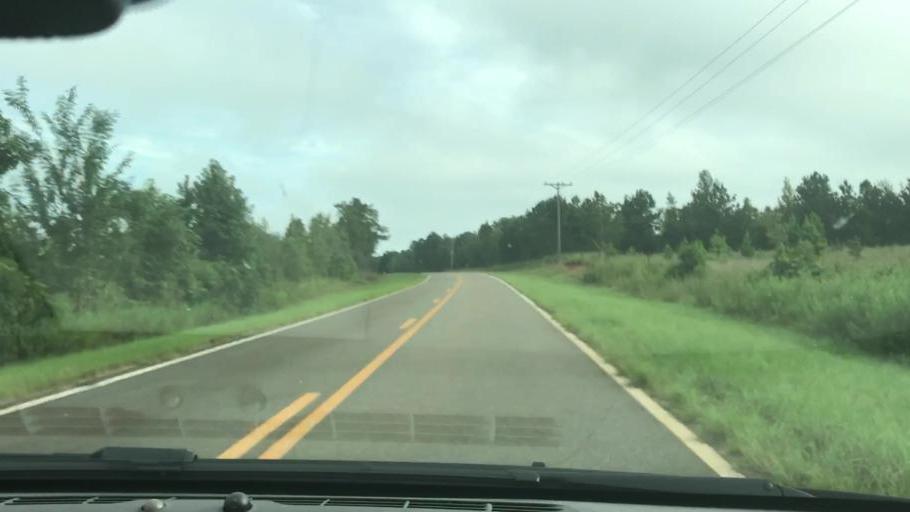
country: US
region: Georgia
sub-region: Stewart County
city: Lumpkin
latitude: 32.0373
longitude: -84.9098
